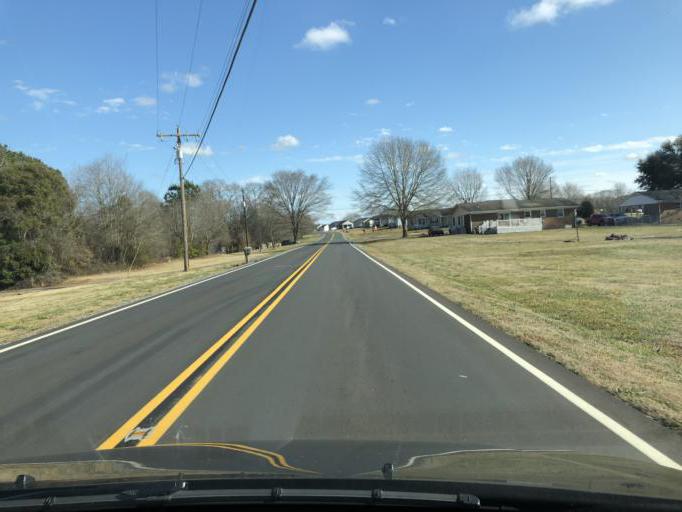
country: US
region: North Carolina
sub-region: Cleveland County
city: Shelby
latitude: 35.2055
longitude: -81.5535
